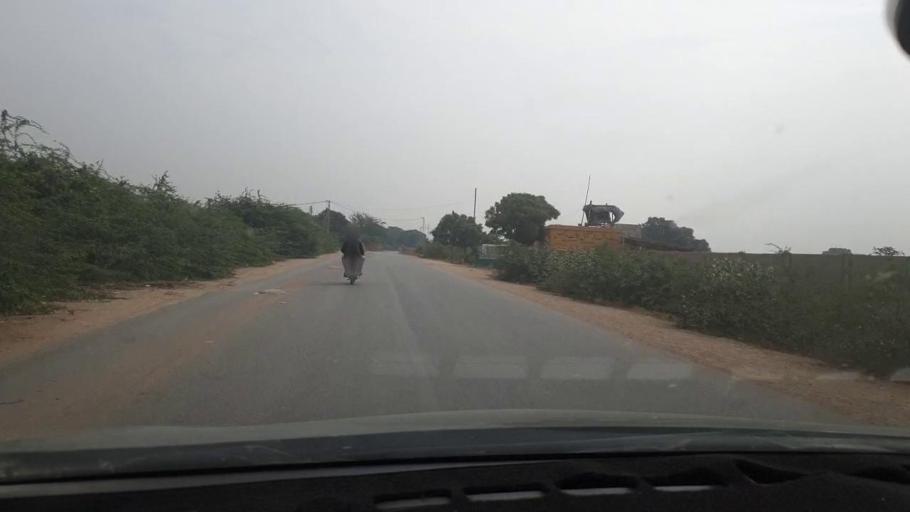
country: PK
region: Sindh
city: Malir Cantonment
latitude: 24.9156
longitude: 67.2607
